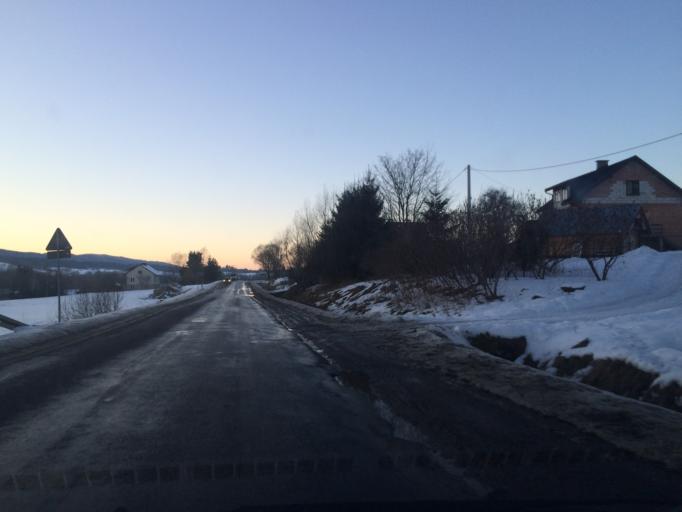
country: PL
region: Subcarpathian Voivodeship
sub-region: Powiat bieszczadzki
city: Czarna
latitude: 49.3676
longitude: 22.6582
